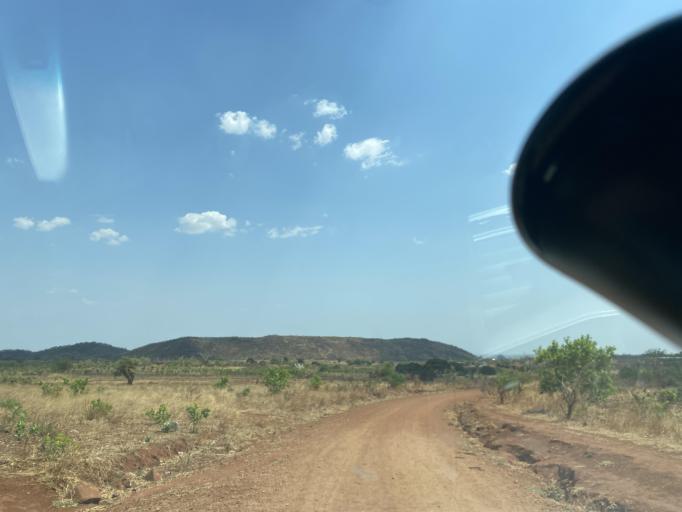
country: ZM
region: Lusaka
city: Lusaka
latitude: -15.5023
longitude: 27.9440
